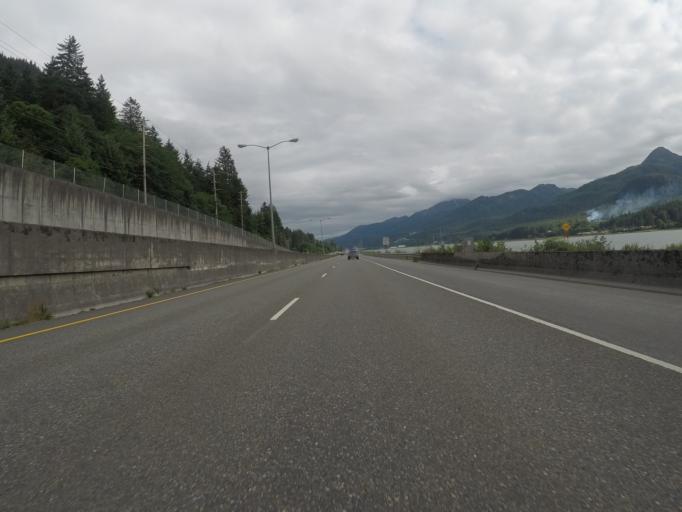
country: US
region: Alaska
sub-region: Juneau City and Borough
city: Juneau
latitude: 58.3235
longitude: -134.4588
